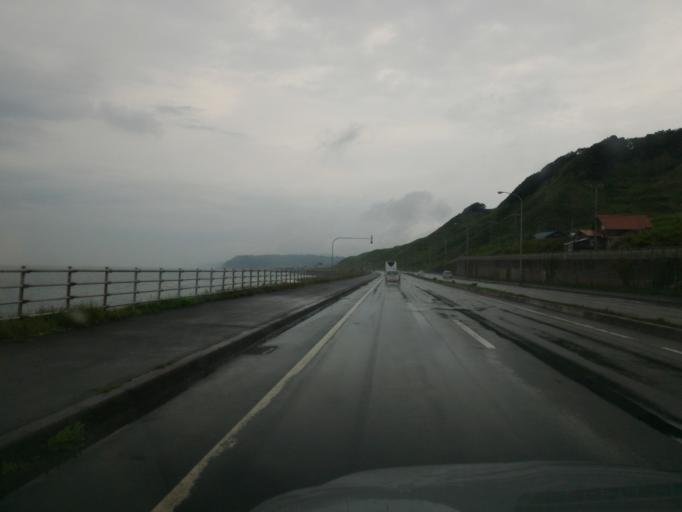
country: JP
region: Hokkaido
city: Rumoi
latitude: 44.0029
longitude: 141.6582
